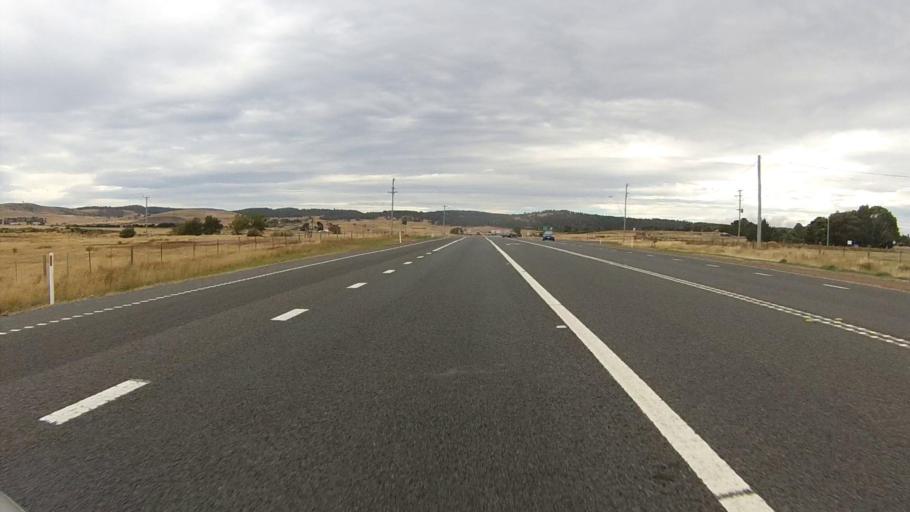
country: AU
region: Tasmania
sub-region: Brighton
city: Bridgewater
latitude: -42.3116
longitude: 147.3571
